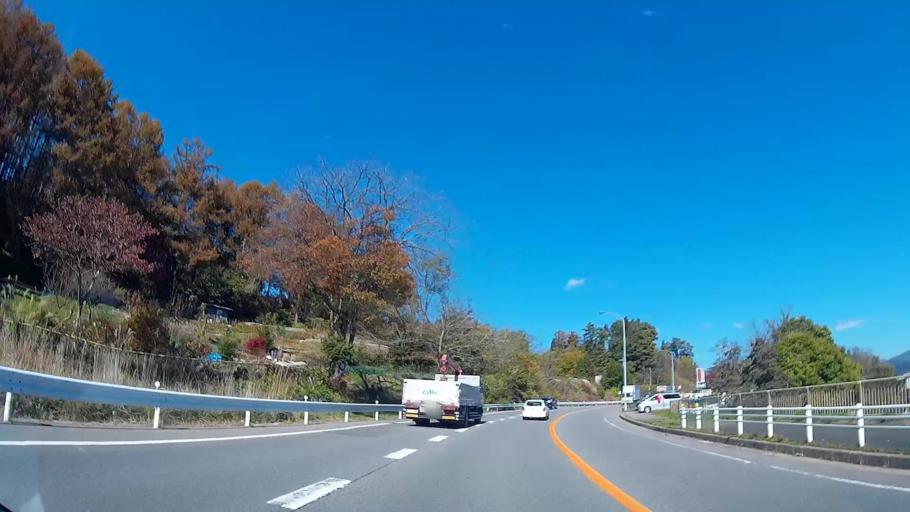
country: JP
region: Nagano
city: Okaya
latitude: 36.0789
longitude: 138.0312
